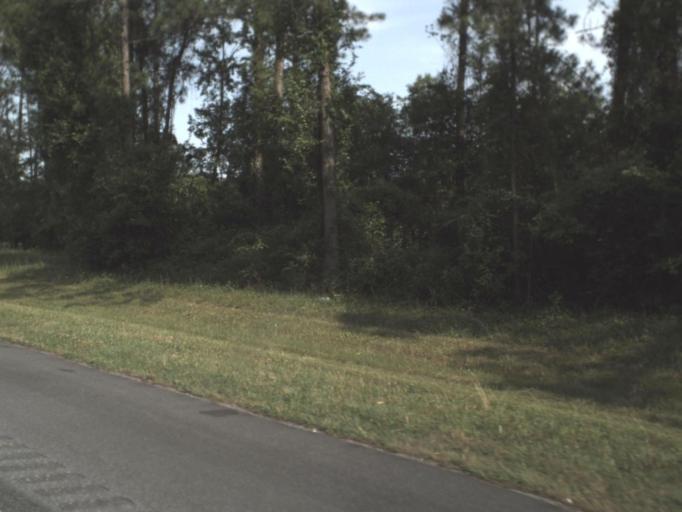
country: US
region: Florida
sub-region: Baker County
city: Macclenny
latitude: 30.2805
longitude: -82.0544
